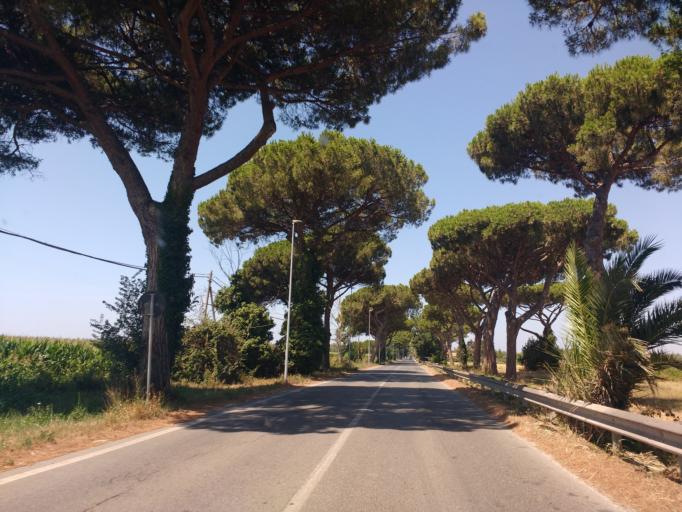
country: IT
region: Latium
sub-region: Citta metropolitana di Roma Capitale
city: Maccarese
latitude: 41.8779
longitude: 12.2114
